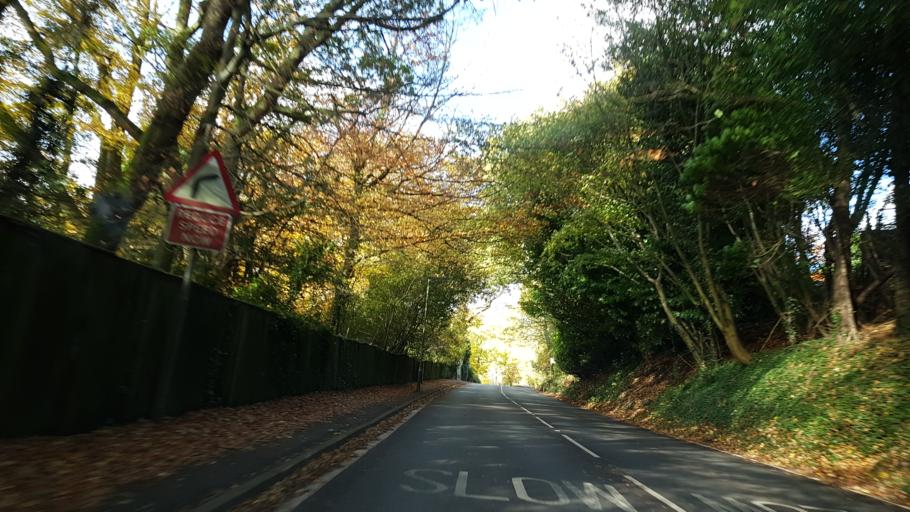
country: GB
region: England
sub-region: Surrey
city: Hindhead
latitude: 51.0886
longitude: -0.7396
